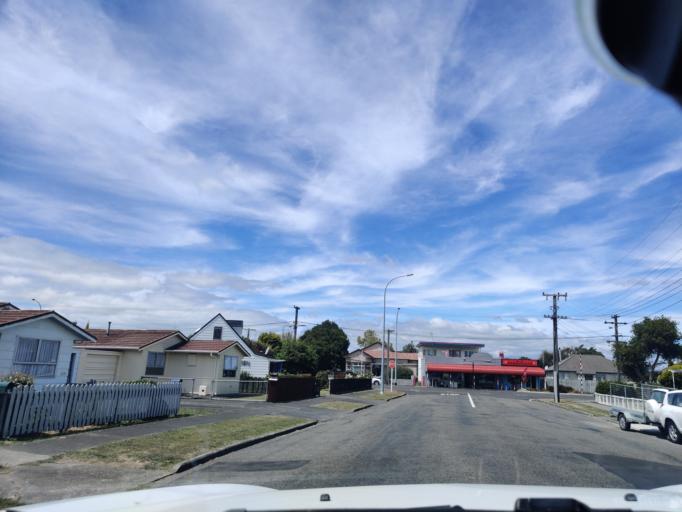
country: NZ
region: Manawatu-Wanganui
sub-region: Horowhenua District
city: Foxton
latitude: -40.4730
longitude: 175.2850
